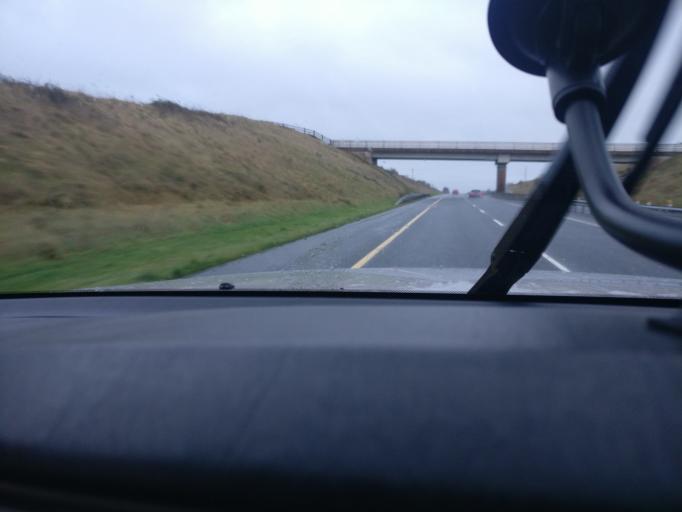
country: IE
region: Leinster
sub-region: An Iarmhi
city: Athlone
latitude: 53.3817
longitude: -8.0512
